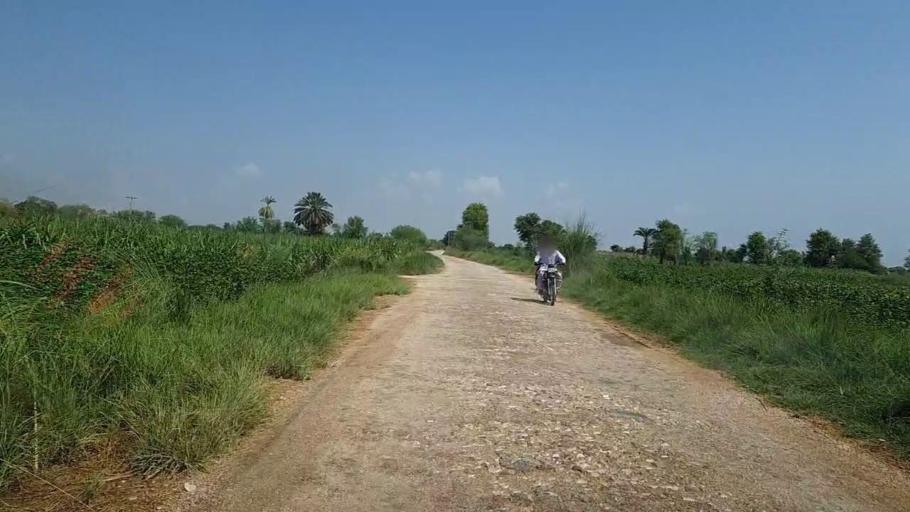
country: PK
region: Sindh
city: Bhiria
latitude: 26.8774
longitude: 68.2460
